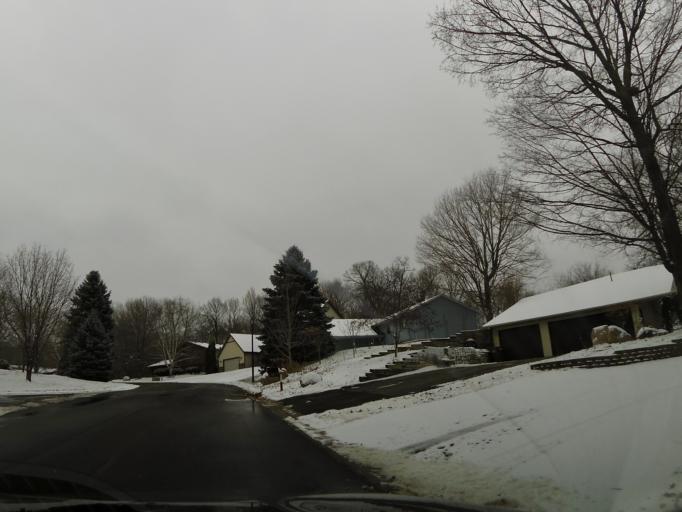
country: US
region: Minnesota
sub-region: Scott County
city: Prior Lake
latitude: 44.7003
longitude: -93.4545
